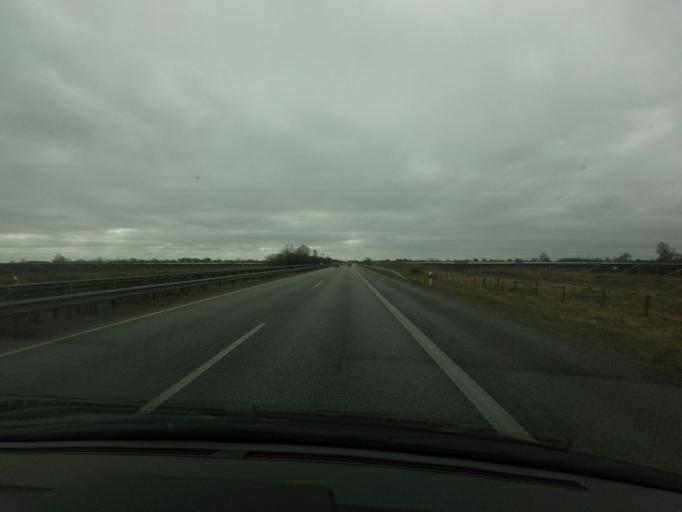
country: DE
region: Schleswig-Holstein
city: Sankelmark
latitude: 54.7163
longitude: 9.3995
